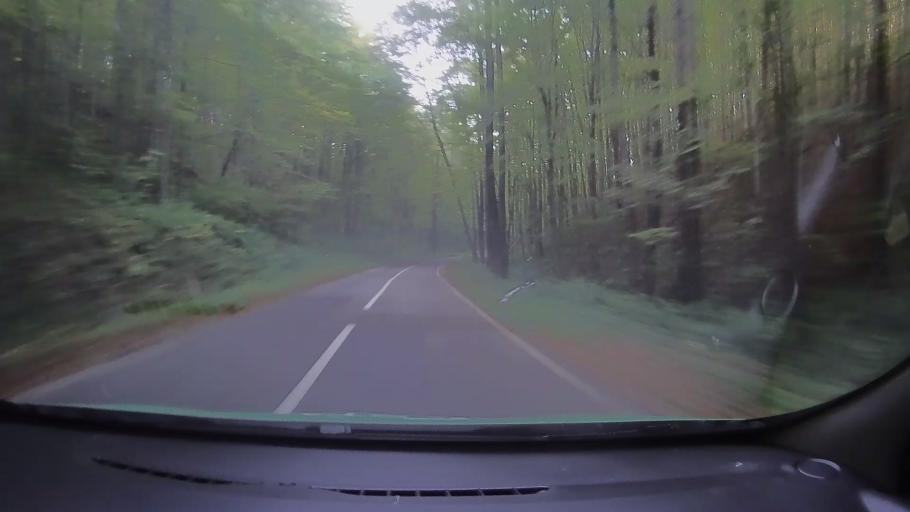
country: RO
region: Timis
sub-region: Comuna Nadrag
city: Nadrag
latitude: 45.6829
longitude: 22.1567
